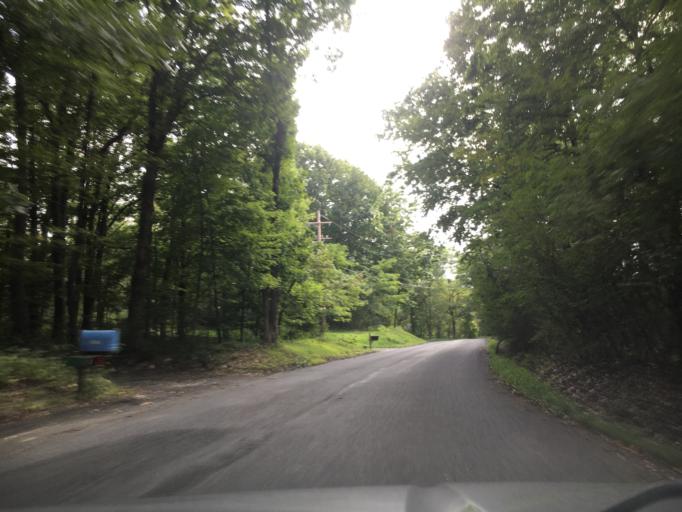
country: US
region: Pennsylvania
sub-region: Berks County
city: Topton
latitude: 40.6125
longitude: -75.7140
